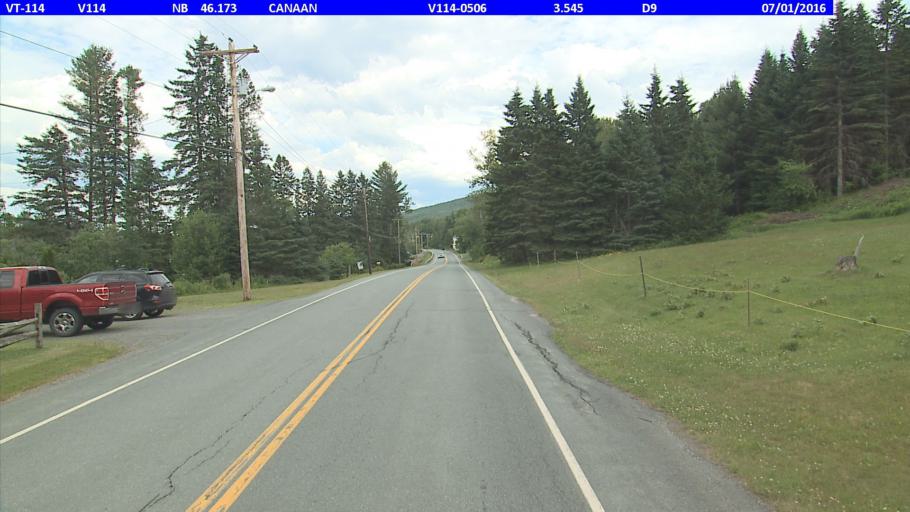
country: US
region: New Hampshire
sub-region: Coos County
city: Colebrook
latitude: 45.0101
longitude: -71.6230
